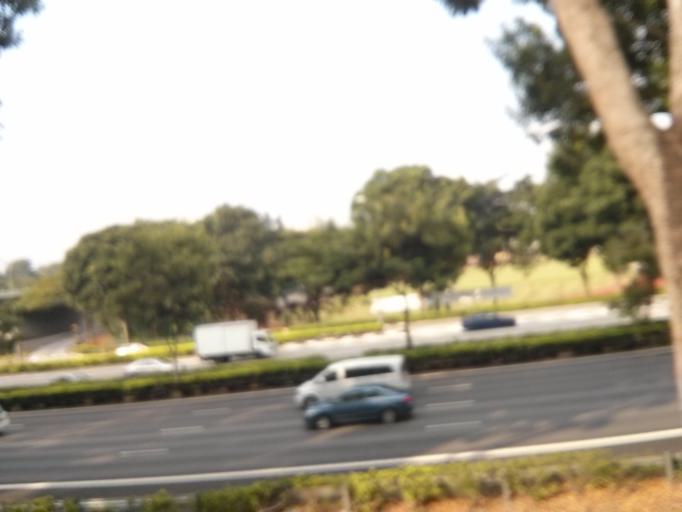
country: SG
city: Singapore
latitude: 1.2883
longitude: 103.7934
